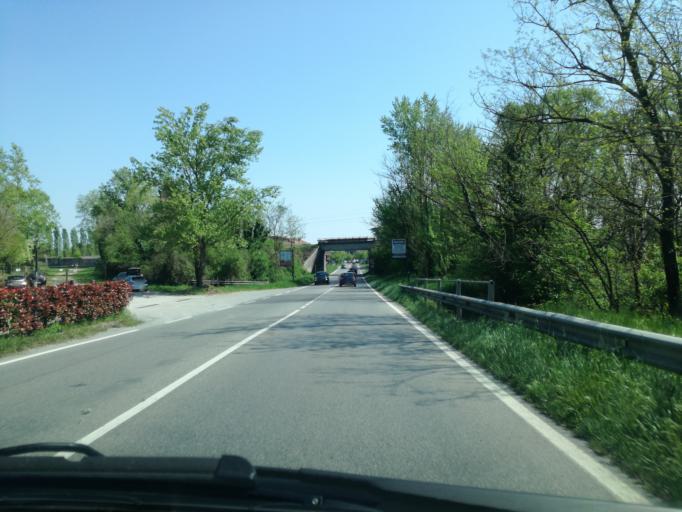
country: IT
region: Lombardy
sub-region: Provincia di Bergamo
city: Terno d'Isola
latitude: 45.6888
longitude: 9.5277
